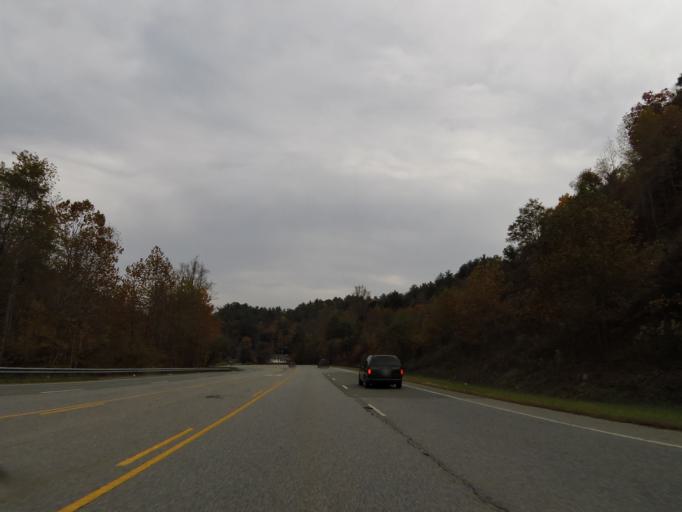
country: US
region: North Carolina
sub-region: Caldwell County
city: Lenoir
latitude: 36.0205
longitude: -81.5756
